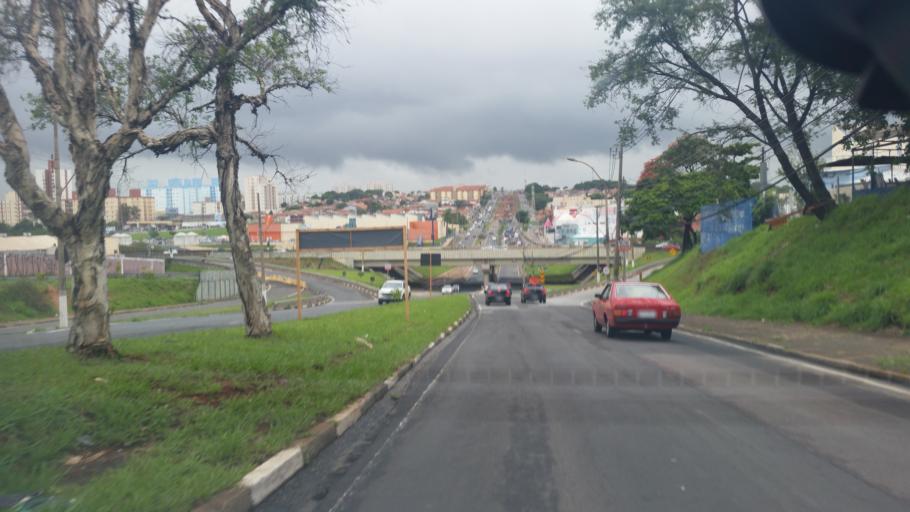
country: BR
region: Sao Paulo
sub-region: Campinas
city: Campinas
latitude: -22.9120
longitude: -47.0985
